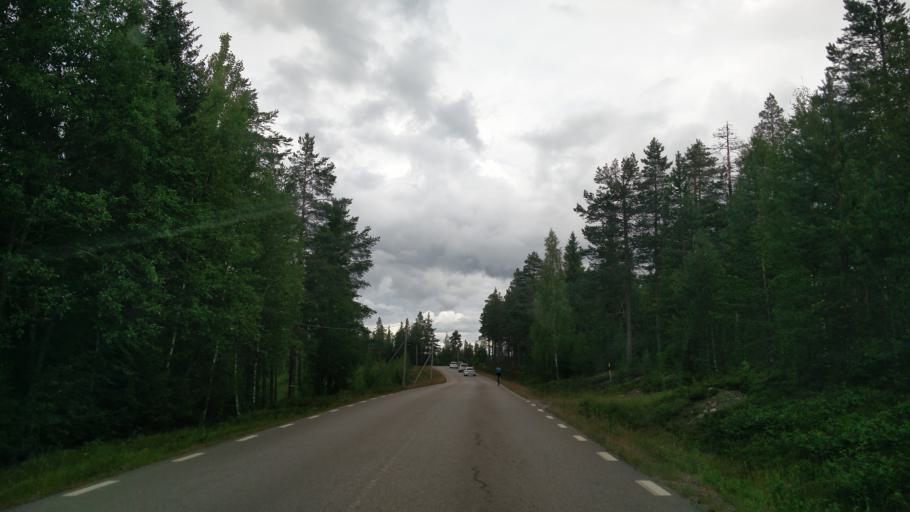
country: NO
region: Hedmark
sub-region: Trysil
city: Innbygda
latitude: 61.1607
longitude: 12.8219
